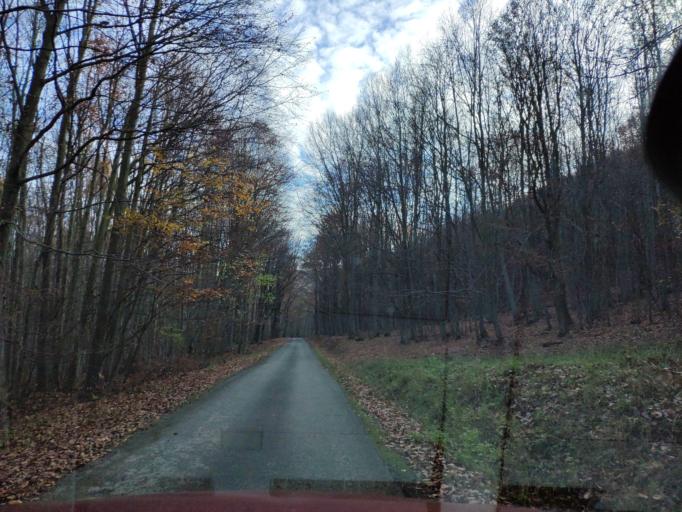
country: HU
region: Borsod-Abauj-Zemplen
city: Gonc
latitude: 48.5948
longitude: 21.4511
